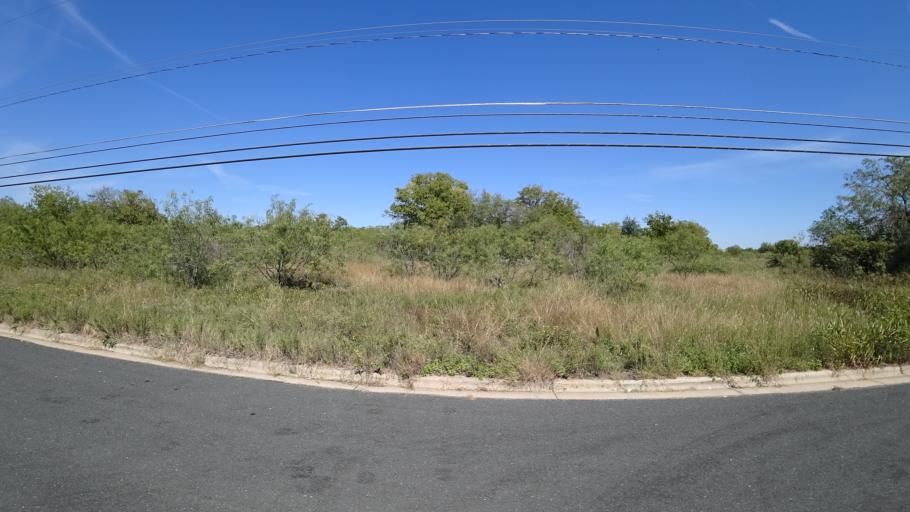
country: US
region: Texas
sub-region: Travis County
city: Austin
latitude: 30.2733
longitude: -97.6750
